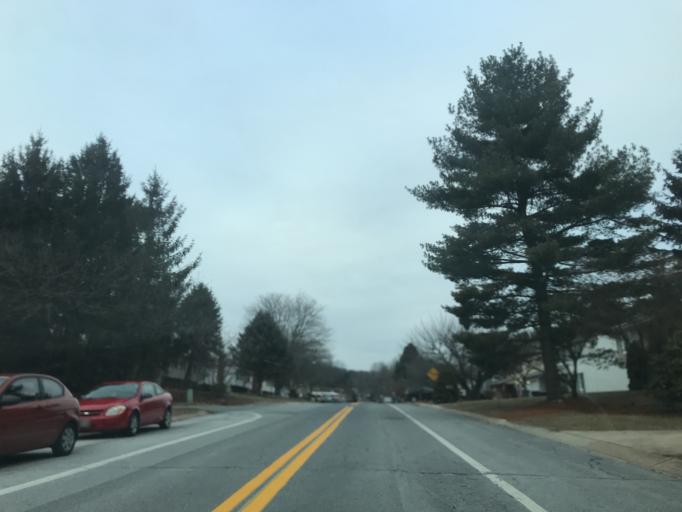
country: US
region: Maryland
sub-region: Carroll County
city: Eldersburg
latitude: 39.3812
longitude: -76.9329
